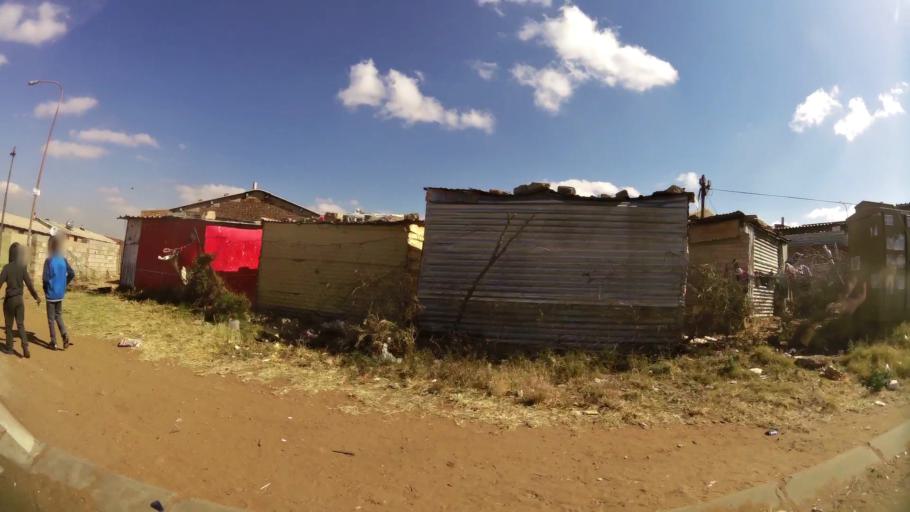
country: ZA
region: Gauteng
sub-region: City of Johannesburg Metropolitan Municipality
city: Soweto
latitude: -26.2229
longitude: 27.8966
